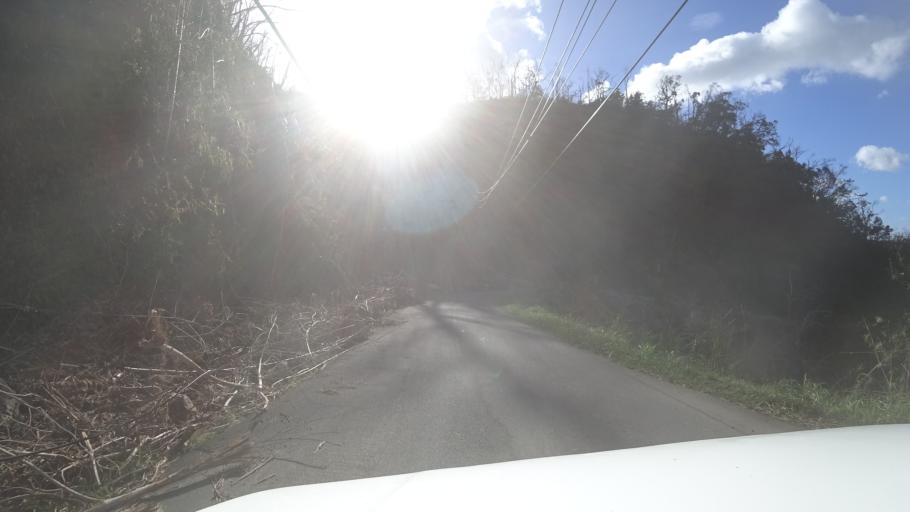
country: DM
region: Saint Luke
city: Pointe Michel
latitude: 15.2726
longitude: -61.3564
